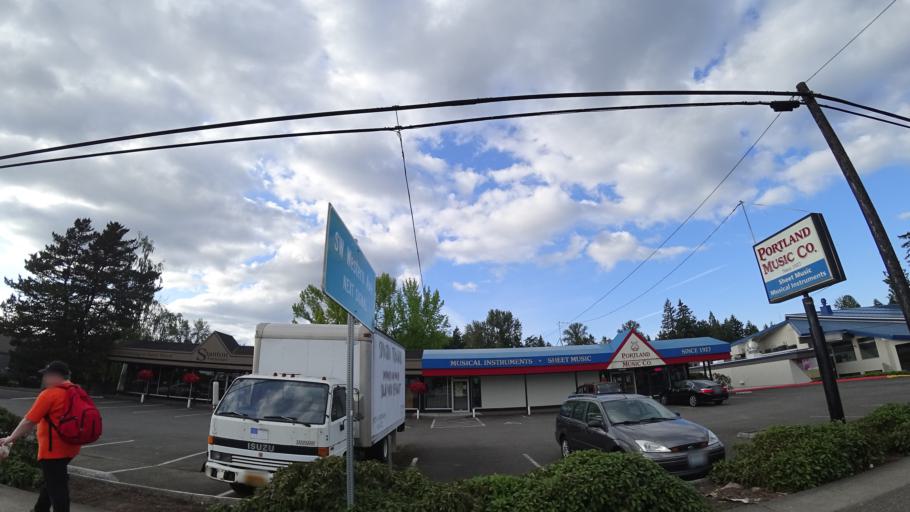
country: US
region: Oregon
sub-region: Washington County
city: Raleigh Hills
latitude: 45.4866
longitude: -122.7808
